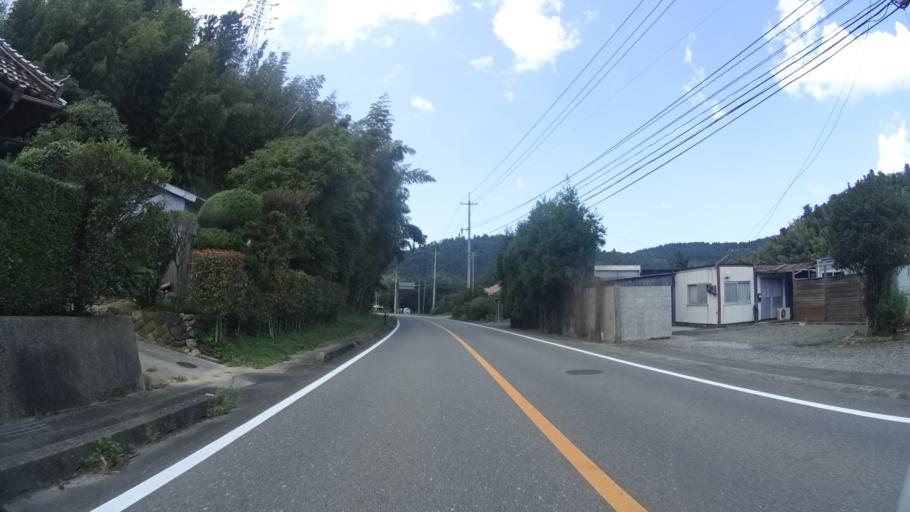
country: JP
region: Yamaguchi
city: Hagi
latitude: 34.4357
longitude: 131.4663
